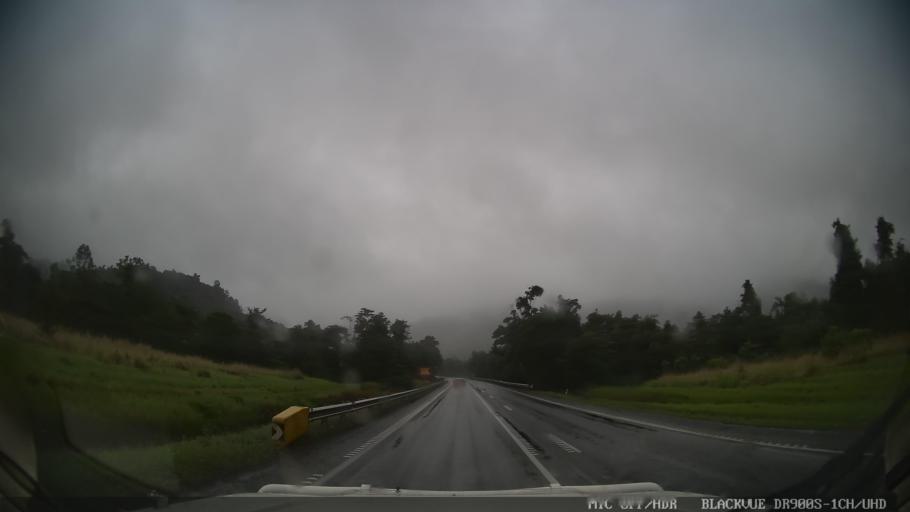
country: AU
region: Queensland
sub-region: Cassowary Coast
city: Innisfail
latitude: -17.8647
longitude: 145.9829
